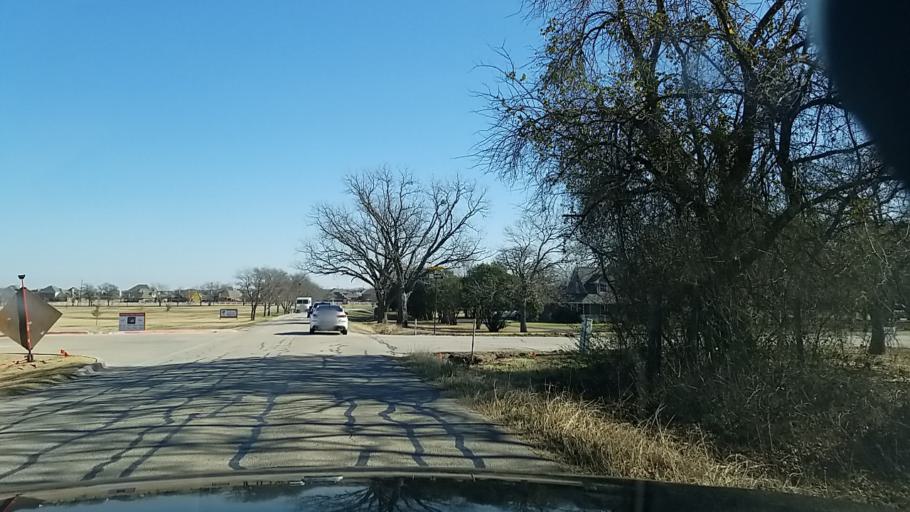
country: US
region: Texas
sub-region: Denton County
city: Argyle
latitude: 33.1309
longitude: -97.1978
